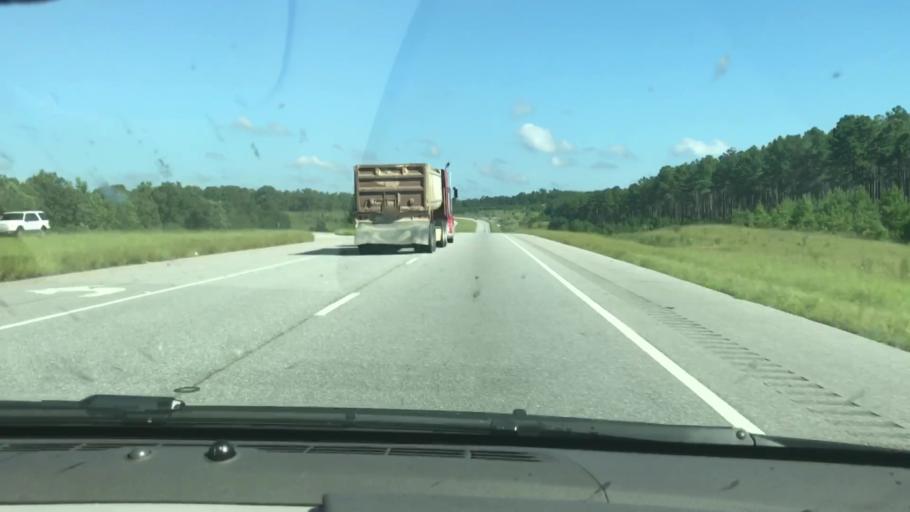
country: US
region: Alabama
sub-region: Barbour County
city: Eufaula
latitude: 32.1217
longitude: -85.1524
